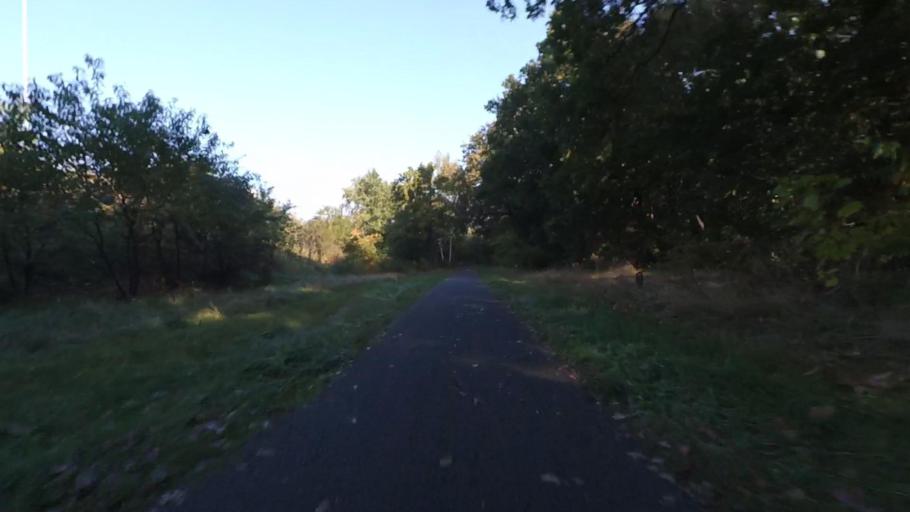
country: NL
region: Gelderland
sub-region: Gemeente Harderwijk
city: Harderwijk
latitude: 52.3359
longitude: 5.6455
